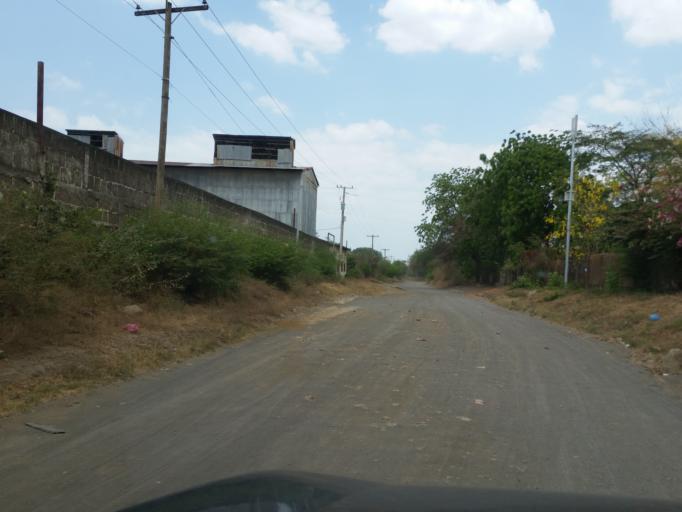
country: NI
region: Managua
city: Managua
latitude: 12.1308
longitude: -86.1643
